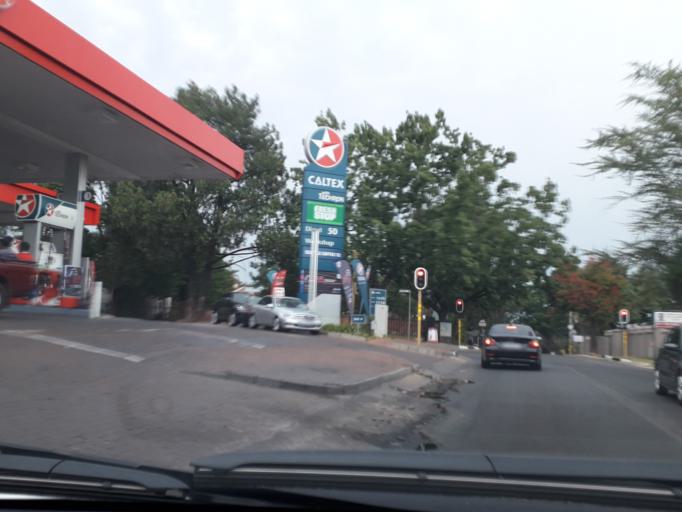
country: ZA
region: Gauteng
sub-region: City of Johannesburg Metropolitan Municipality
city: Johannesburg
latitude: -26.0927
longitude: 28.0360
